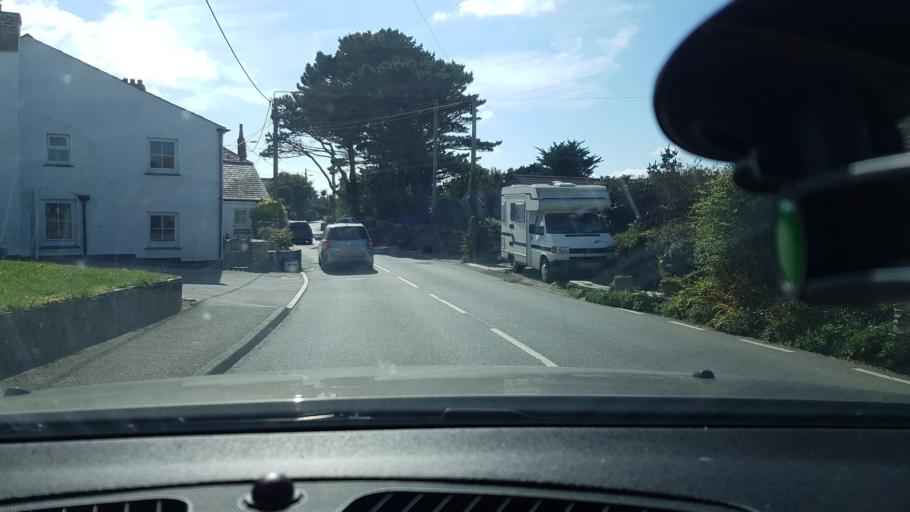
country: GB
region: England
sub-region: Cornwall
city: Tintagel
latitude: 50.6681
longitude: -4.7361
